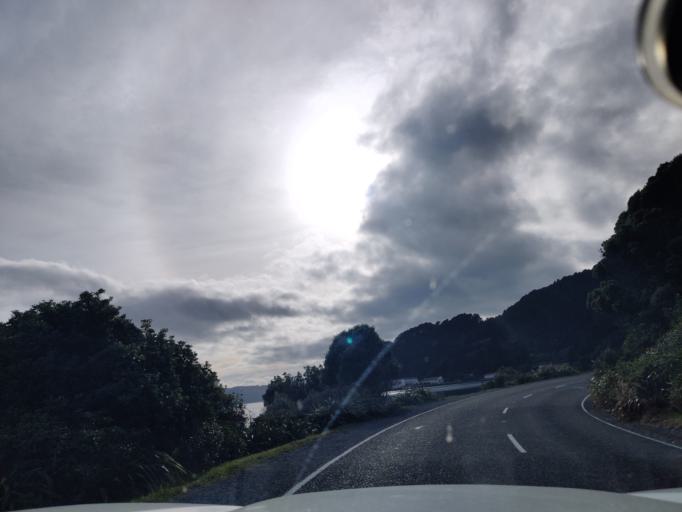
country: NZ
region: Wellington
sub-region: Wellington City
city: Wellington
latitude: -41.2994
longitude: 174.8173
